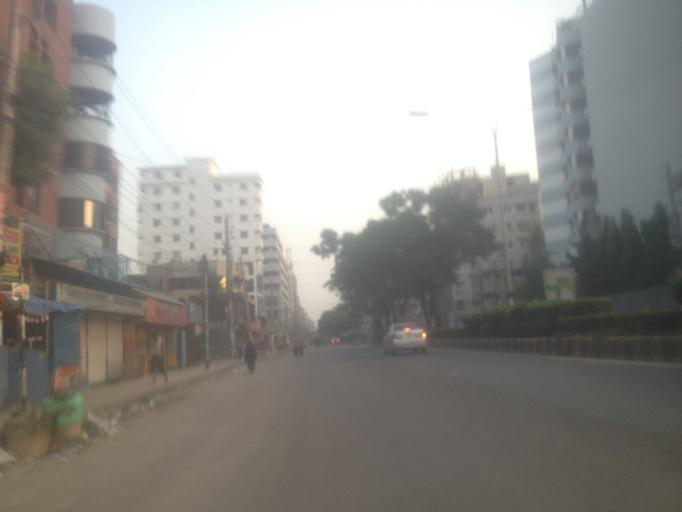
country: BD
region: Dhaka
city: Azimpur
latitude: 23.7881
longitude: 90.3767
